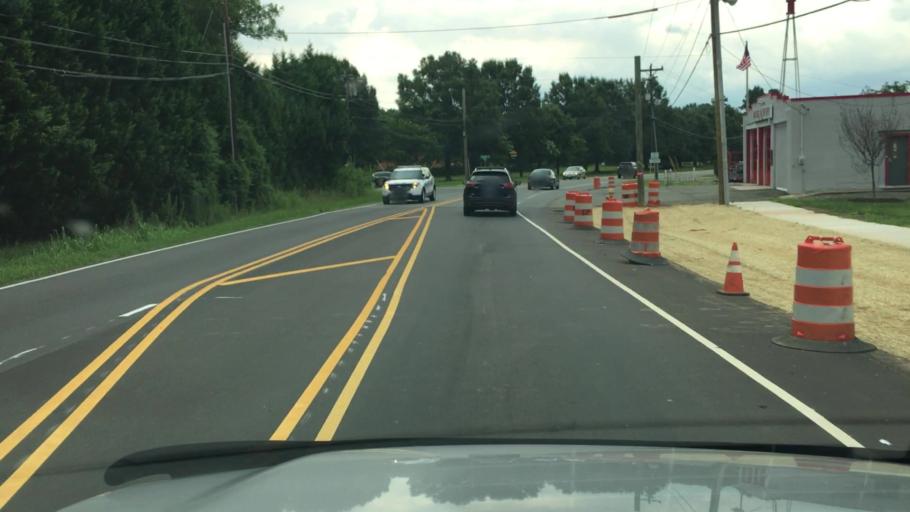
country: US
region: North Carolina
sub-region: Mecklenburg County
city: Huntersville
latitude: 35.3259
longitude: -80.8673
